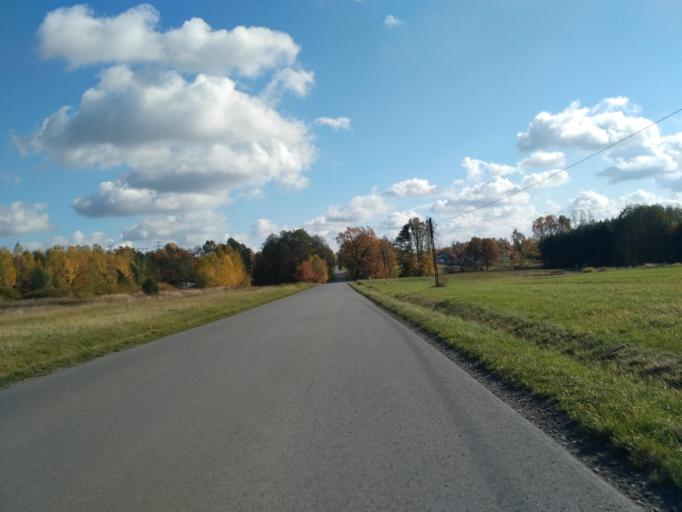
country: PL
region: Subcarpathian Voivodeship
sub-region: Powiat rzeszowski
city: Glogow Malopolski
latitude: 50.1593
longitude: 21.9119
